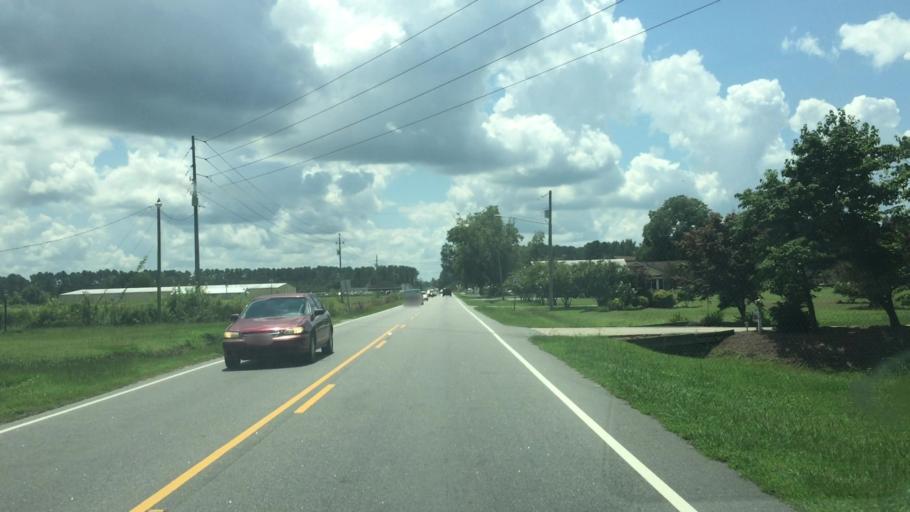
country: US
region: North Carolina
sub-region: Columbus County
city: Chadbourn
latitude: 34.3430
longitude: -78.8272
